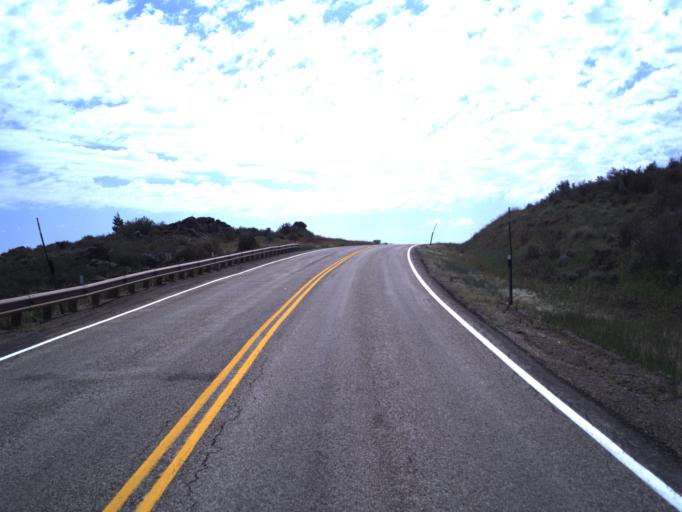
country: US
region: Utah
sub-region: Daggett County
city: Manila
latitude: 40.8913
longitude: -109.7111
